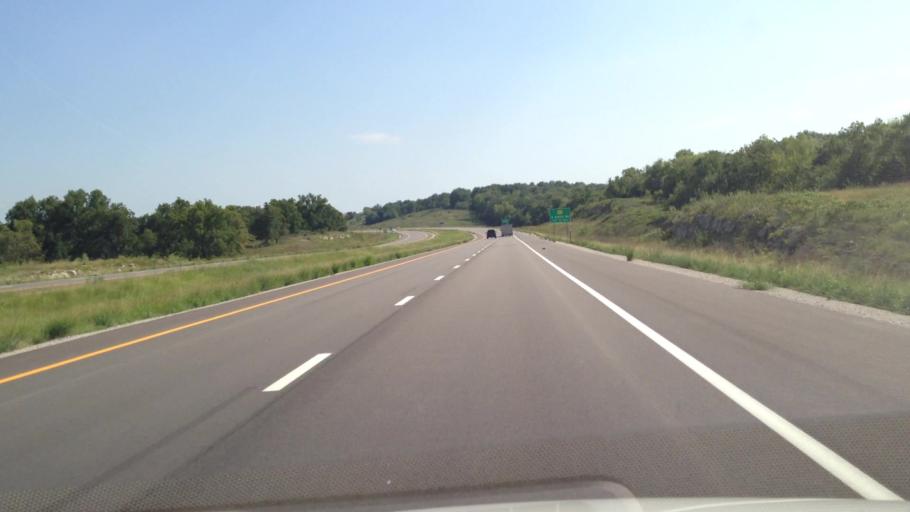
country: US
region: Kansas
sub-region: Linn County
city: La Cygne
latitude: 38.3598
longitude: -94.6876
